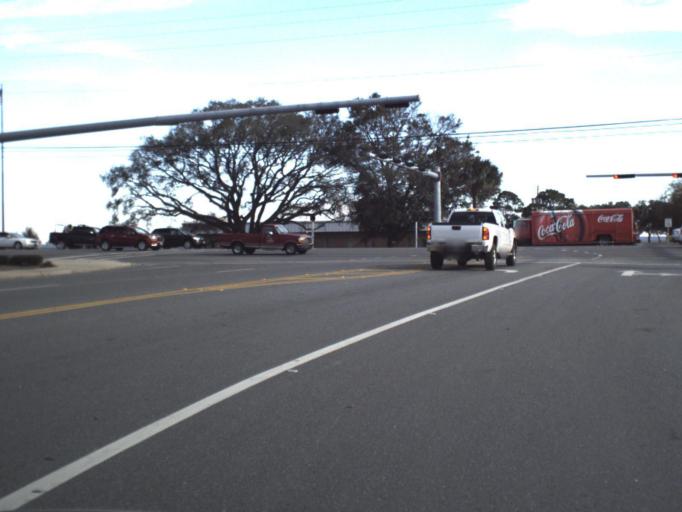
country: US
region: Florida
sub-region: Bay County
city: Upper Grand Lagoon
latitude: 30.1846
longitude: -85.7311
